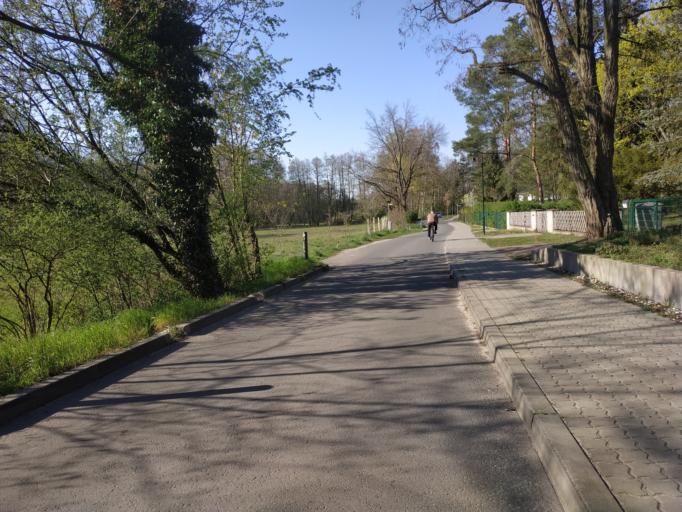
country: DE
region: Brandenburg
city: Petershagen
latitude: 52.5481
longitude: 13.8245
